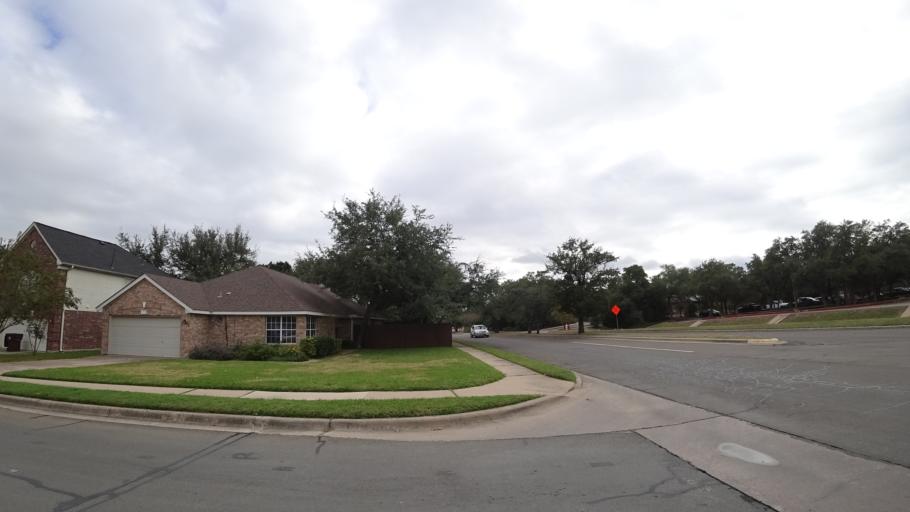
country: US
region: Texas
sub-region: Williamson County
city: Brushy Creek
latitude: 30.5116
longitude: -97.7105
